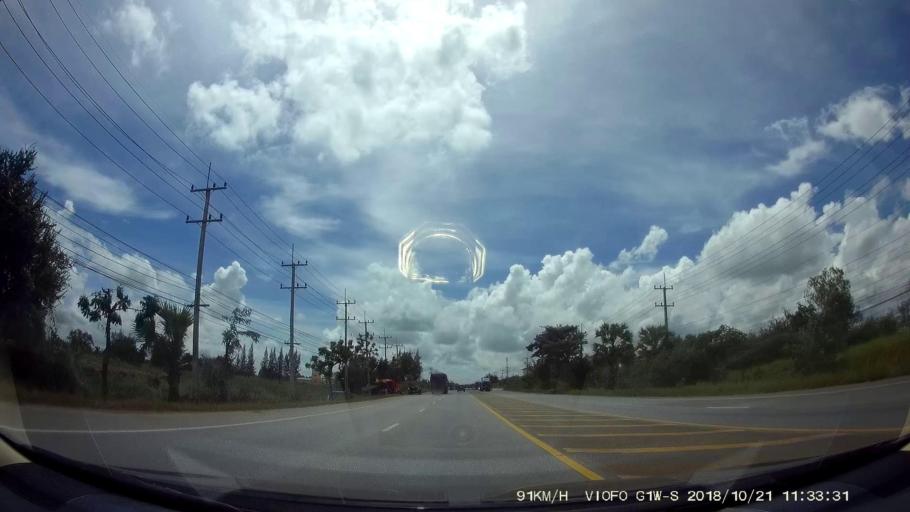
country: TH
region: Chaiyaphum
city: Chaiyaphum
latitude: 15.7447
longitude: 102.0242
